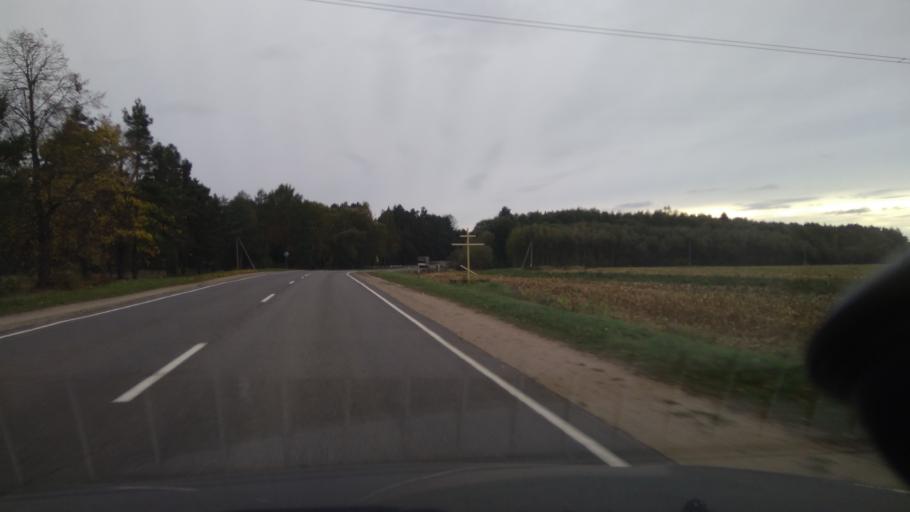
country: BY
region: Minsk
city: Svislach
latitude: 53.6511
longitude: 27.9290
